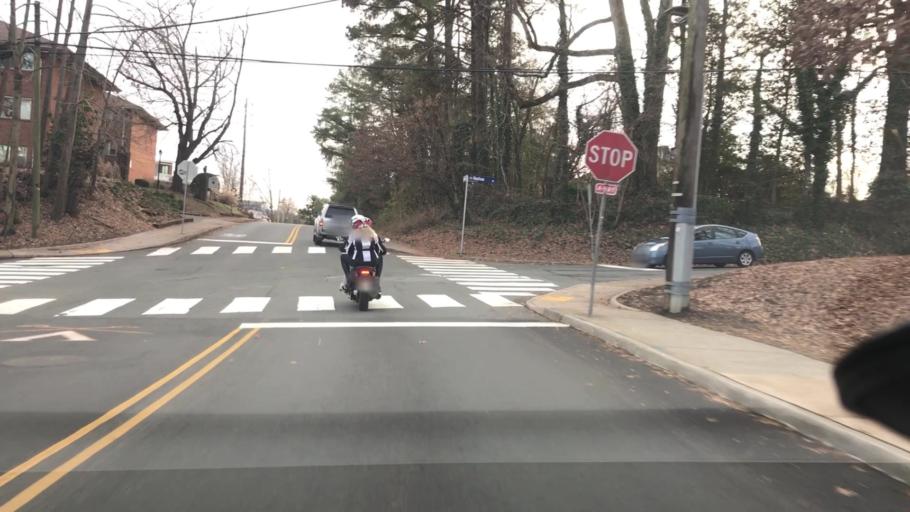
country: US
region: Virginia
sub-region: City of Charlottesville
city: Charlottesville
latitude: 38.0289
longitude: -78.5166
